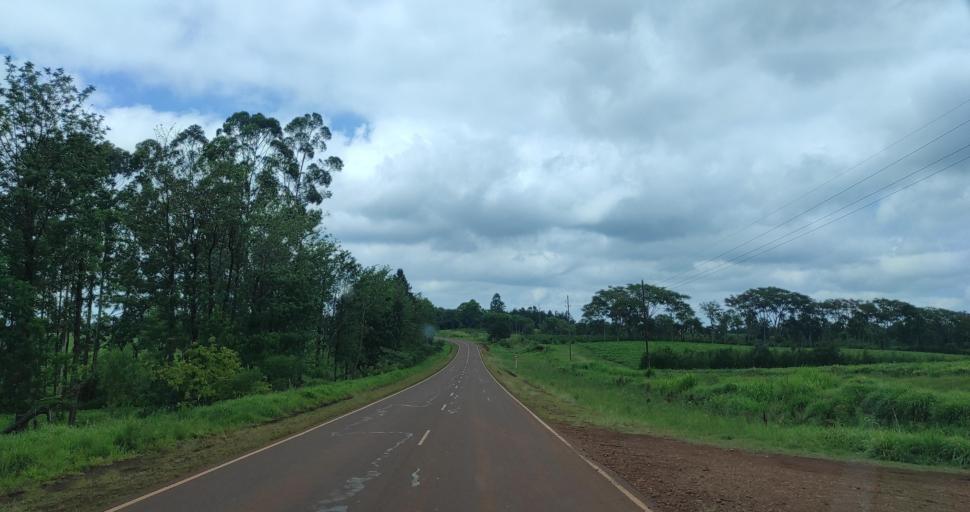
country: AR
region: Misiones
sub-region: Departamento de Veinticinco de Mayo
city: Veinticinco de Mayo
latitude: -27.4008
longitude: -54.7501
